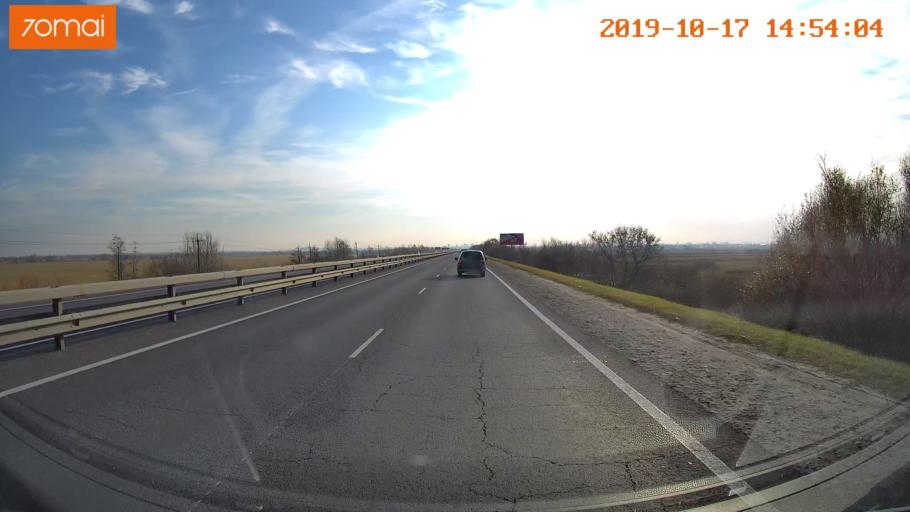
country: RU
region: Rjazan
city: Polyany
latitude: 54.6863
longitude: 39.8346
